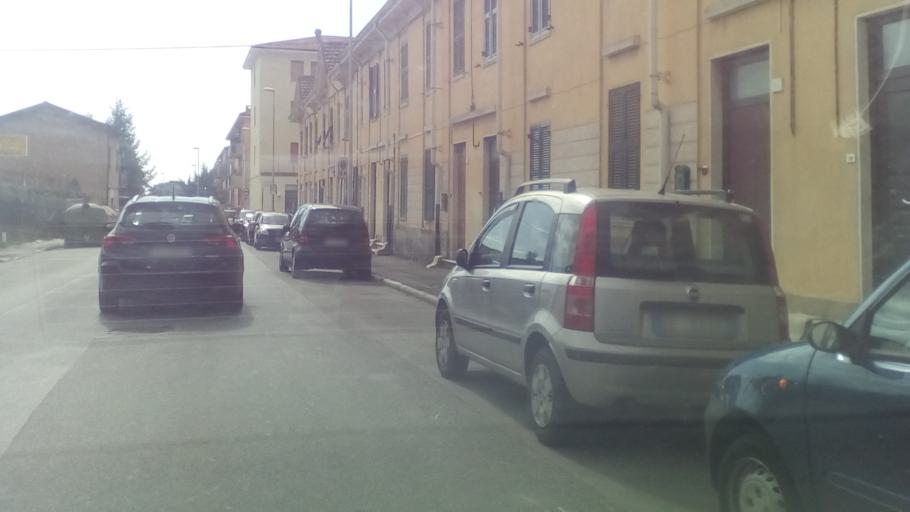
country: IT
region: Tuscany
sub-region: Provincia di Massa-Carrara
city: Carrara
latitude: 44.0640
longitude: 10.0770
